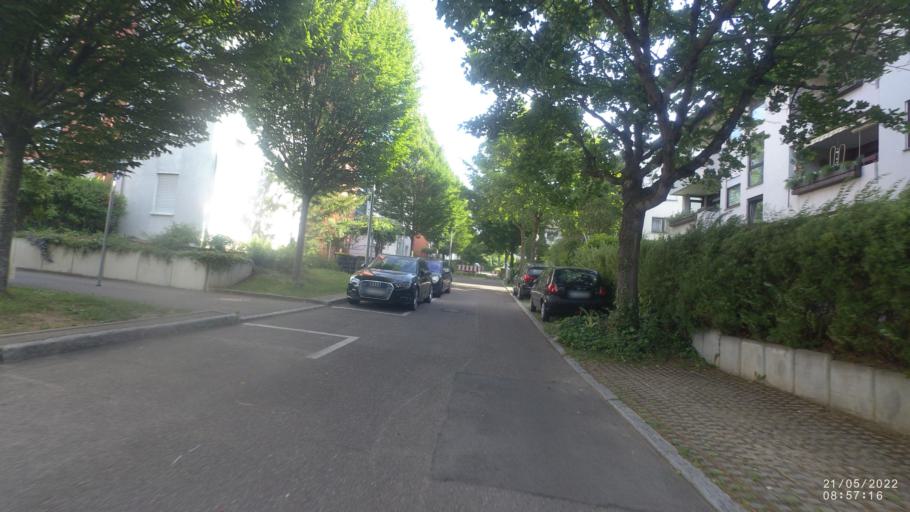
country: DE
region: Baden-Wuerttemberg
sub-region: Regierungsbezirk Stuttgart
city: Fellbach
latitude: 48.8282
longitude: 9.2699
